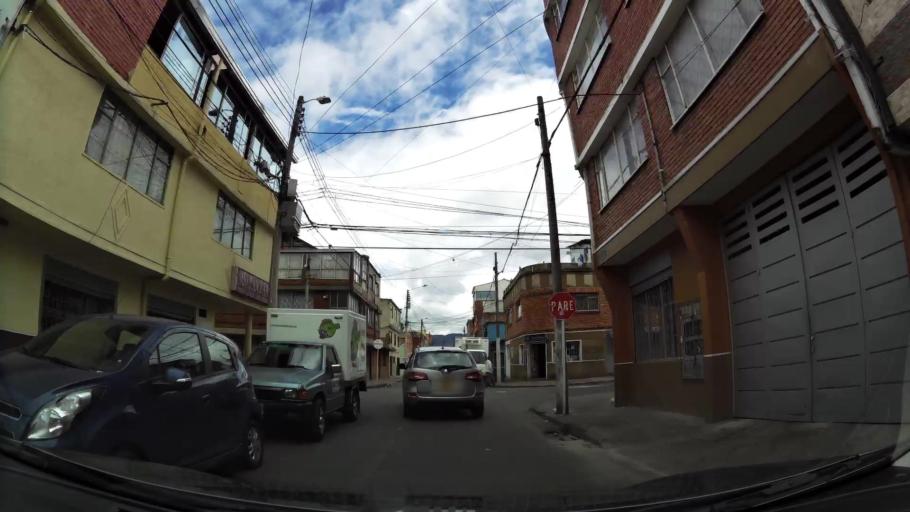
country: CO
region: Bogota D.C.
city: Barrio San Luis
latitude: 4.6974
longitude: -74.1032
